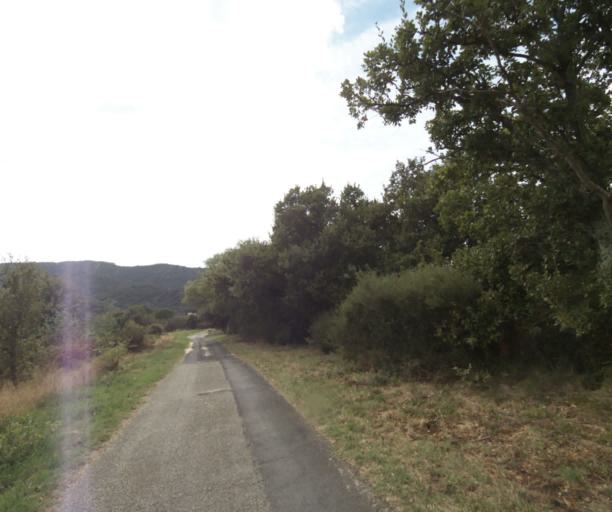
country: FR
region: Languedoc-Roussillon
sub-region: Departement des Pyrenees-Orientales
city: Argelers
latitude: 42.5341
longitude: 3.0147
